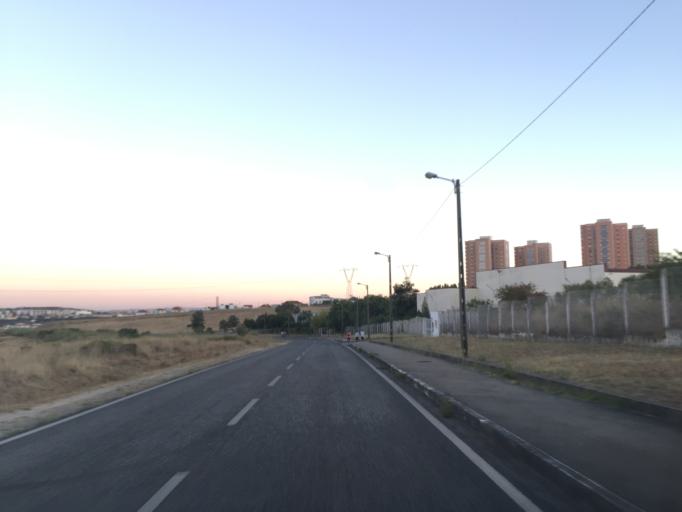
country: PT
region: Lisbon
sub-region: Odivelas
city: Povoa de Santo Adriao
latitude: 38.8135
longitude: -9.1751
